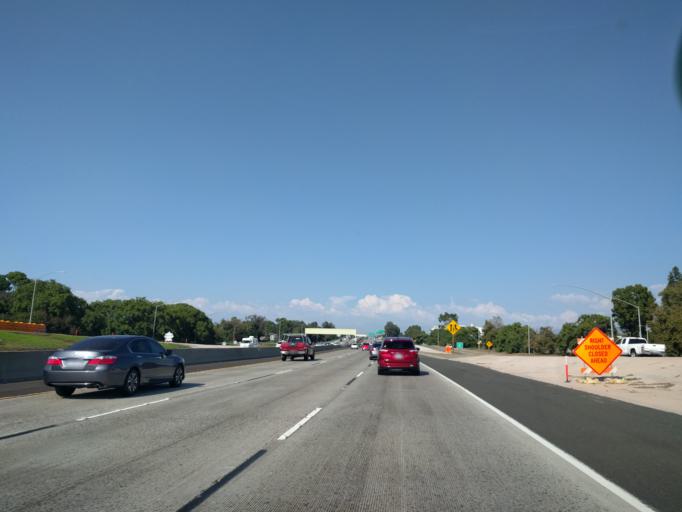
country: US
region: California
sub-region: Orange County
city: Costa Mesa
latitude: 33.6755
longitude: -117.8834
